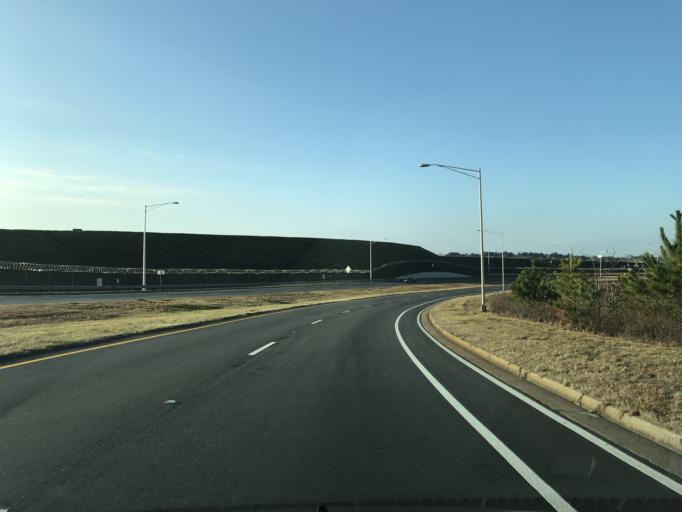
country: US
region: Georgia
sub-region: Fulton County
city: College Park
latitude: 33.6231
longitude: -84.4464
